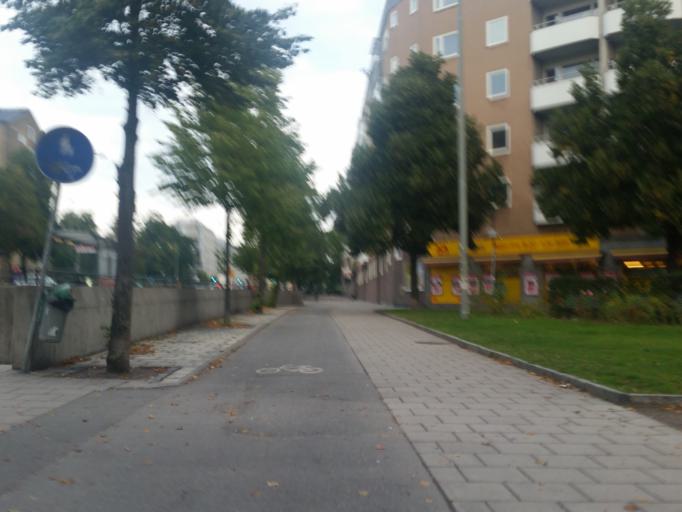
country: SE
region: Stockholm
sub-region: Stockholms Kommun
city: Arsta
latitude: 59.3089
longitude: 18.0643
